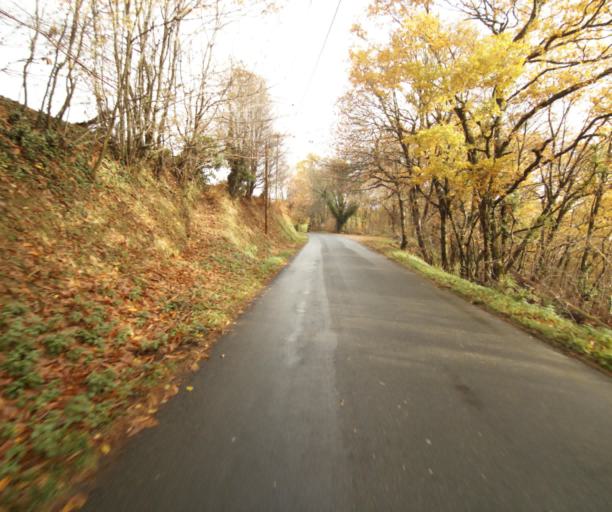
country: FR
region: Limousin
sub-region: Departement de la Correze
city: Cornil
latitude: 45.2077
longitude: 1.6416
